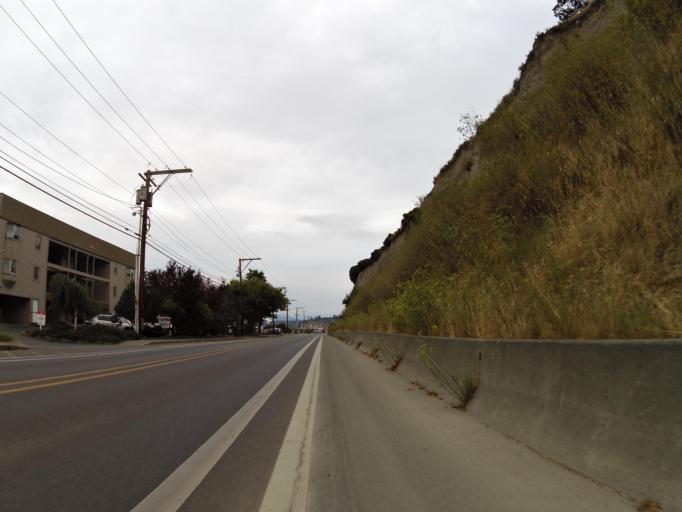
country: US
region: Washington
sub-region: Jefferson County
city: Port Townsend
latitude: 48.1112
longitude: -122.7645
